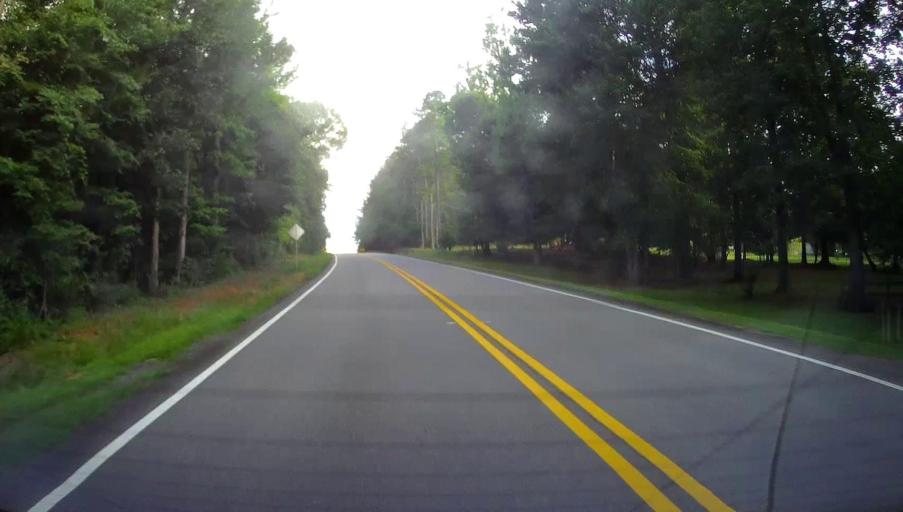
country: US
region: Georgia
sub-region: Crawford County
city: Knoxville
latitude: 32.8816
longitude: -83.9961
